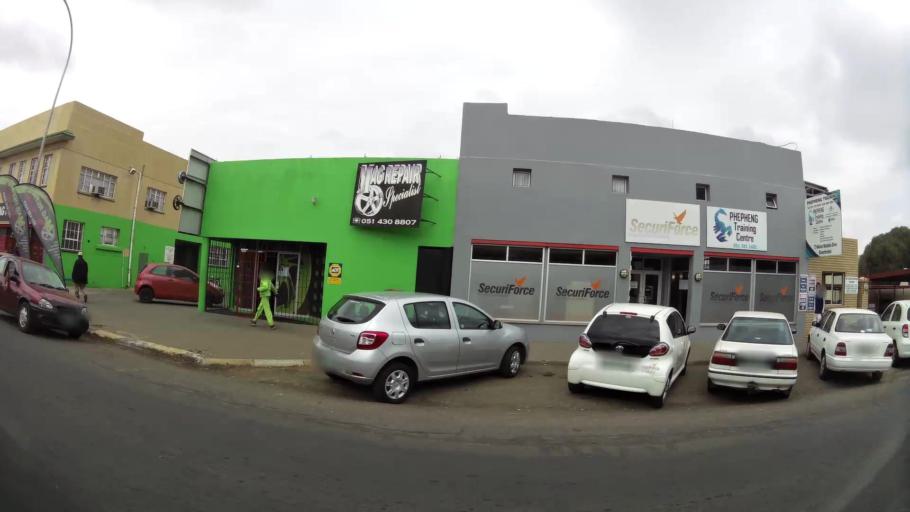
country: ZA
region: Orange Free State
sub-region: Mangaung Metropolitan Municipality
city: Bloemfontein
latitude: -29.1141
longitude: 26.2205
